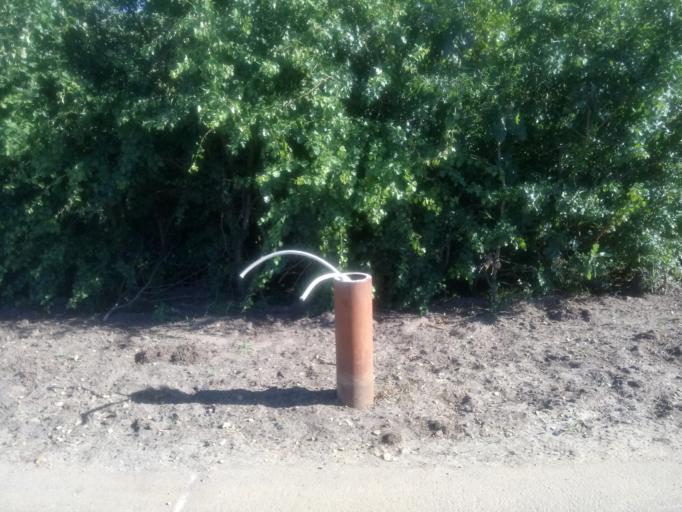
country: DK
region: Central Jutland
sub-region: Herning Kommune
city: Herning
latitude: 56.1506
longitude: 8.9747
